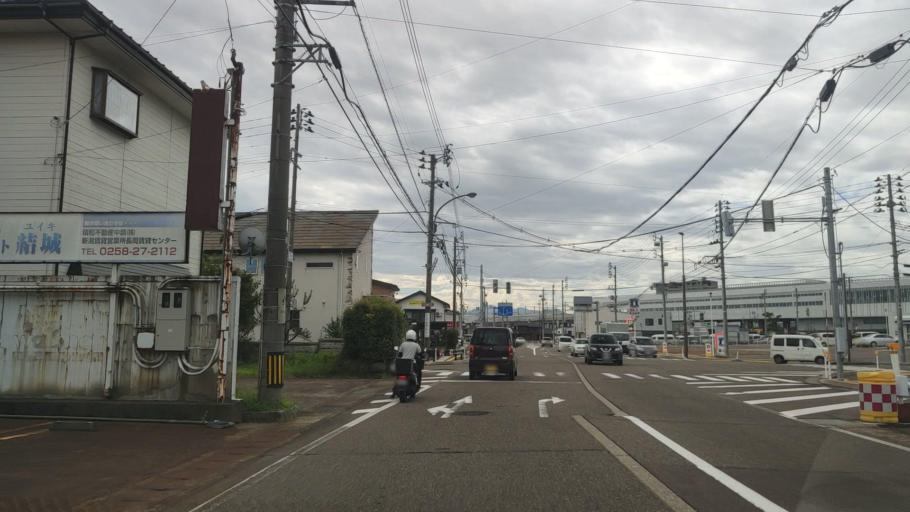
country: JP
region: Niigata
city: Joetsu
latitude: 37.0840
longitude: 138.2501
